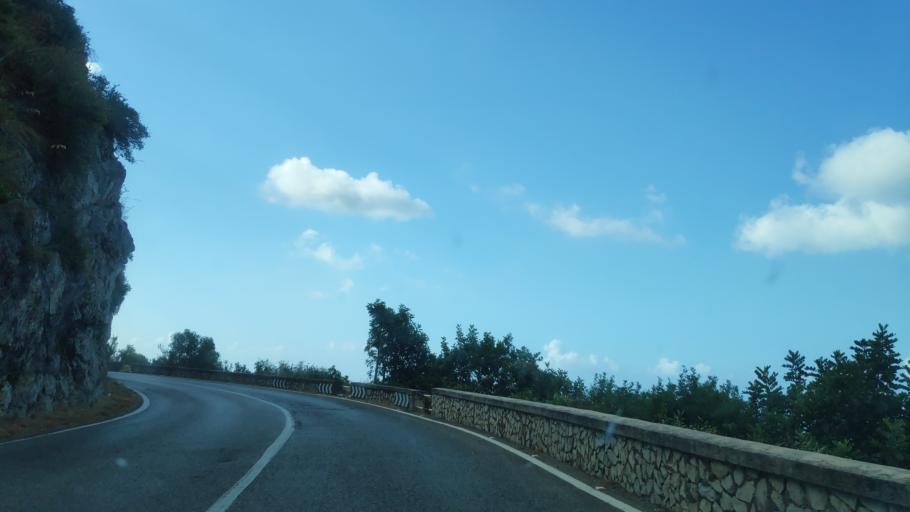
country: IT
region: Campania
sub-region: Provincia di Salerno
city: Positano
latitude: 40.6199
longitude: 14.4596
